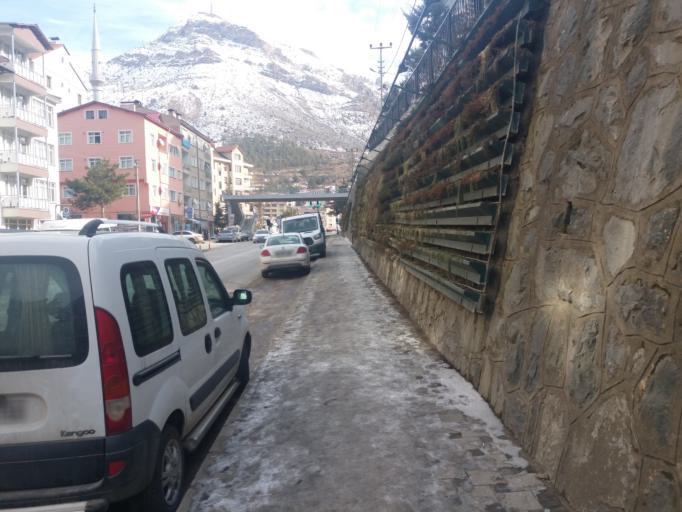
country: TR
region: Gumushane
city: Gumushkhane
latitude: 40.4573
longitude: 39.4826
